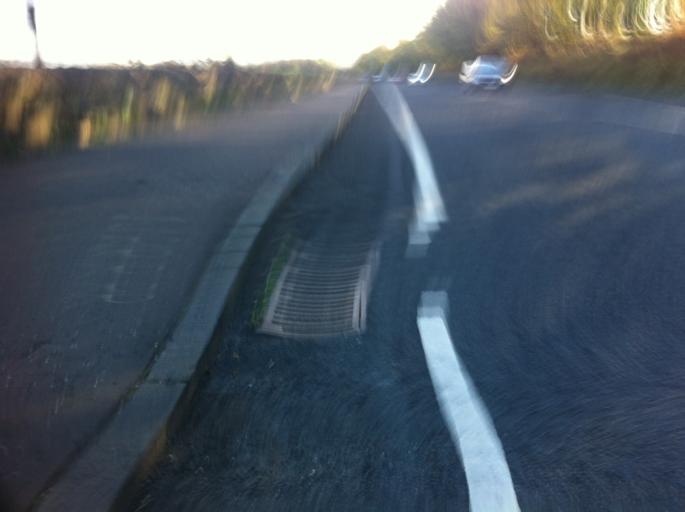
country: GB
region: Scotland
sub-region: East Dunbartonshire
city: Bishopbriggs
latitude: 55.9289
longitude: -4.1966
